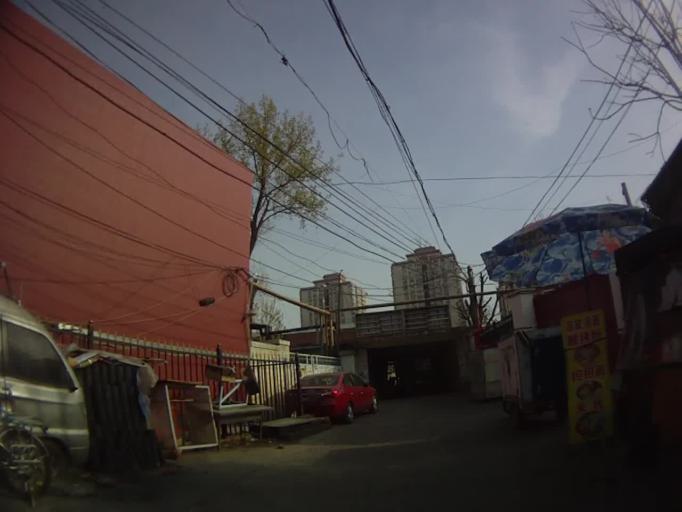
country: CN
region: Beijing
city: Chaowai
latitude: 39.9011
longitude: 116.4426
